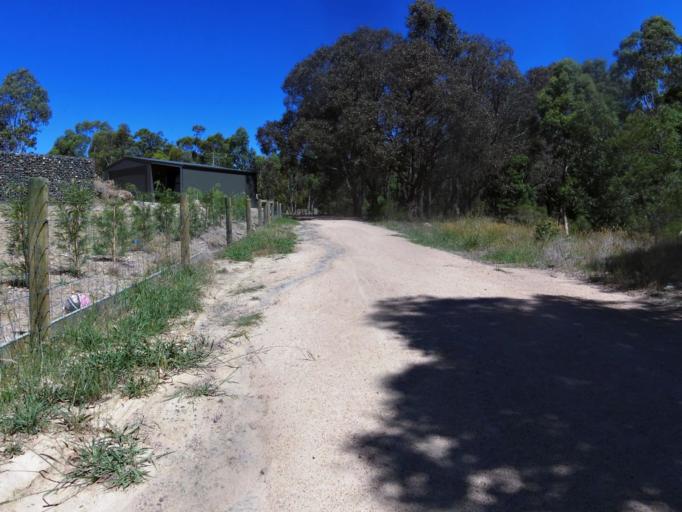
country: AU
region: Victoria
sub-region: Whittlesea
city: Whittlesea
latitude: -37.3664
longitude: 145.0367
